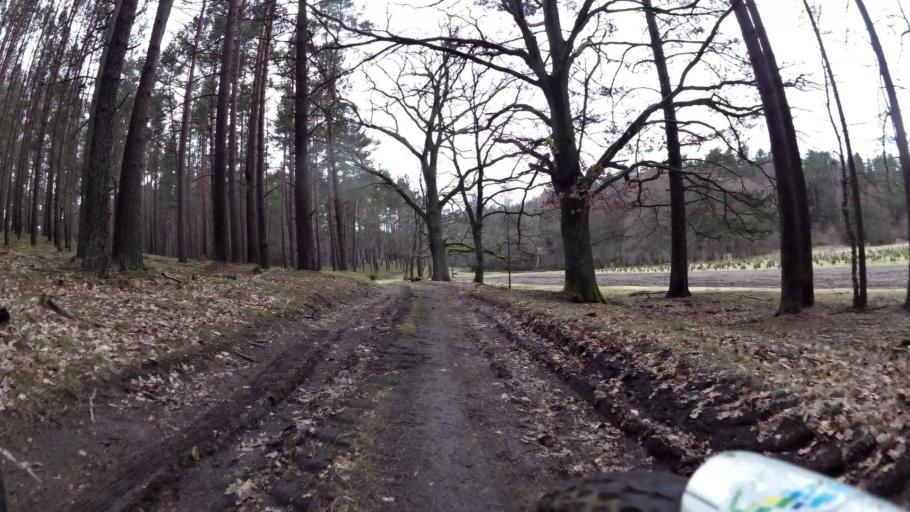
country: PL
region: Pomeranian Voivodeship
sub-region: Powiat bytowski
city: Trzebielino
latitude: 54.1493
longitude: 17.1597
